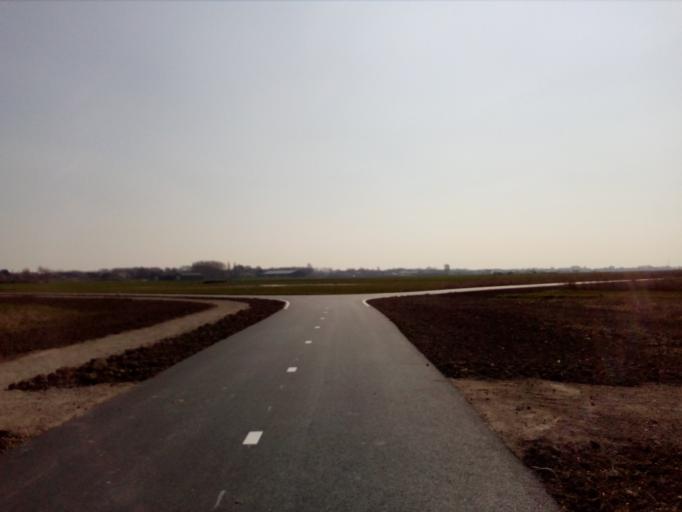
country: NL
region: South Holland
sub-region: Gemeente Waddinxveen
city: Groenswaard
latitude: 52.0688
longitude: 4.6292
